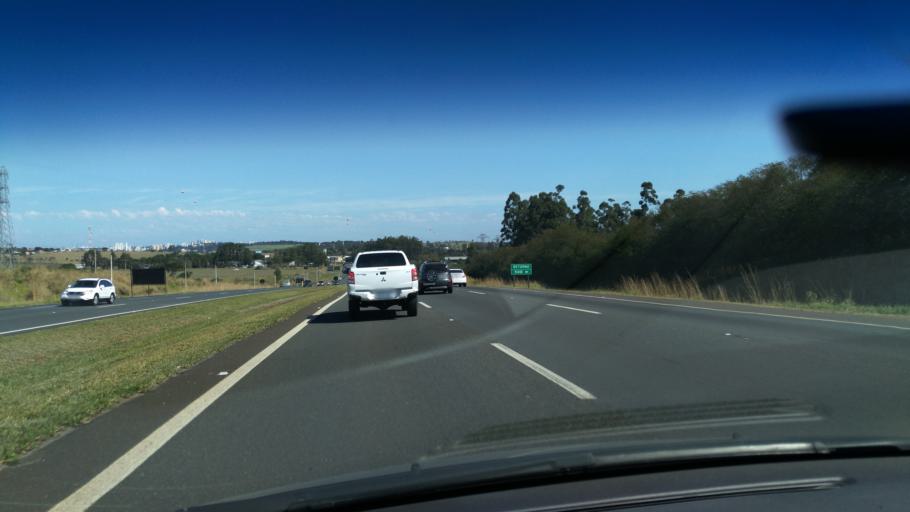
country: BR
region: Sao Paulo
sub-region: Jaguariuna
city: Jaguariuna
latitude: -22.7797
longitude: -47.0248
